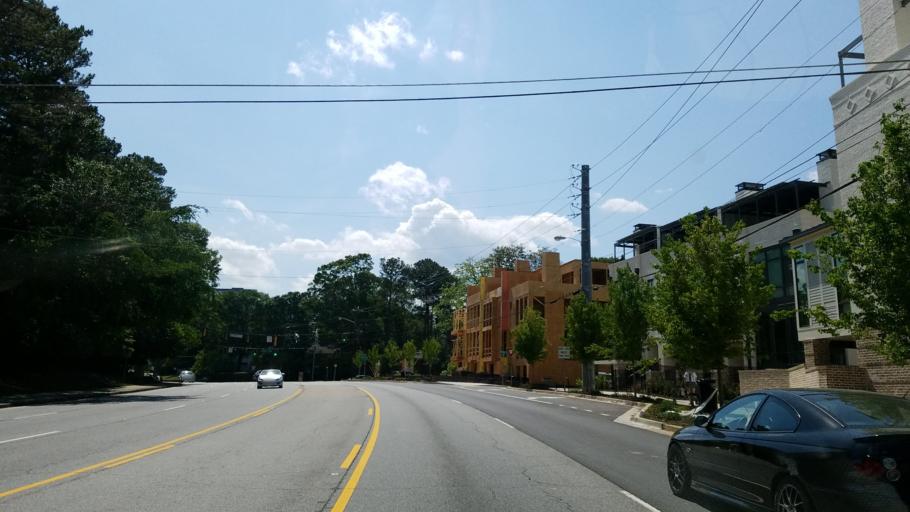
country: US
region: Georgia
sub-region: DeKalb County
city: North Atlanta
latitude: 33.8579
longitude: -84.3471
